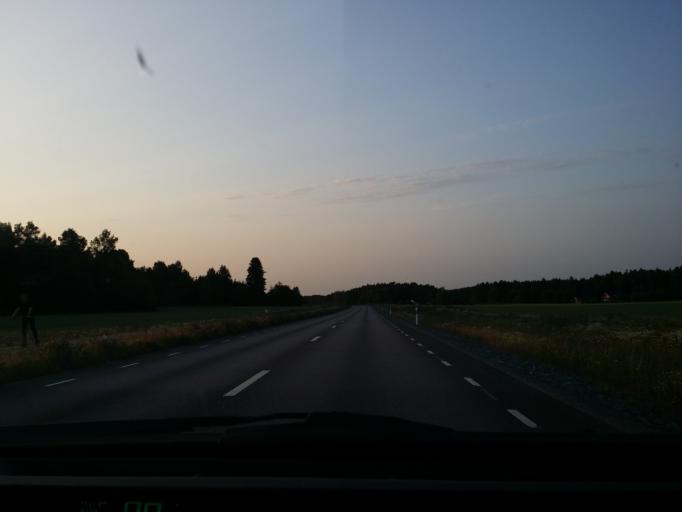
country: SE
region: Vaestmanland
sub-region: Vasteras
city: Tillberga
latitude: 59.5878
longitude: 16.6658
